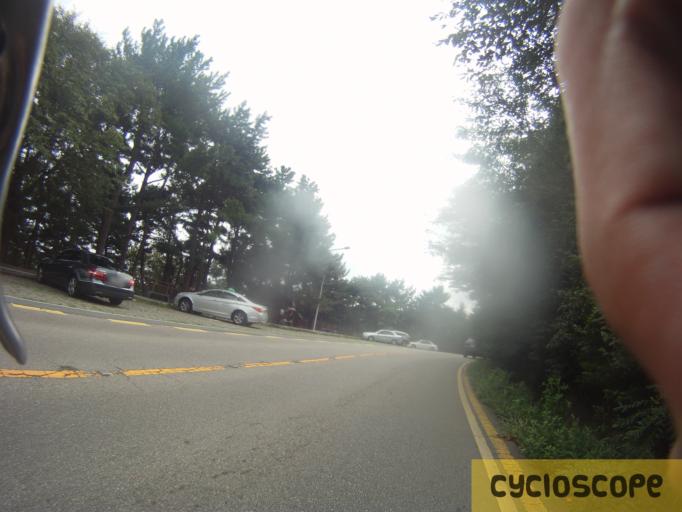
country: KR
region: Busan
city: Kijang
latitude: 35.1689
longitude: 129.1906
